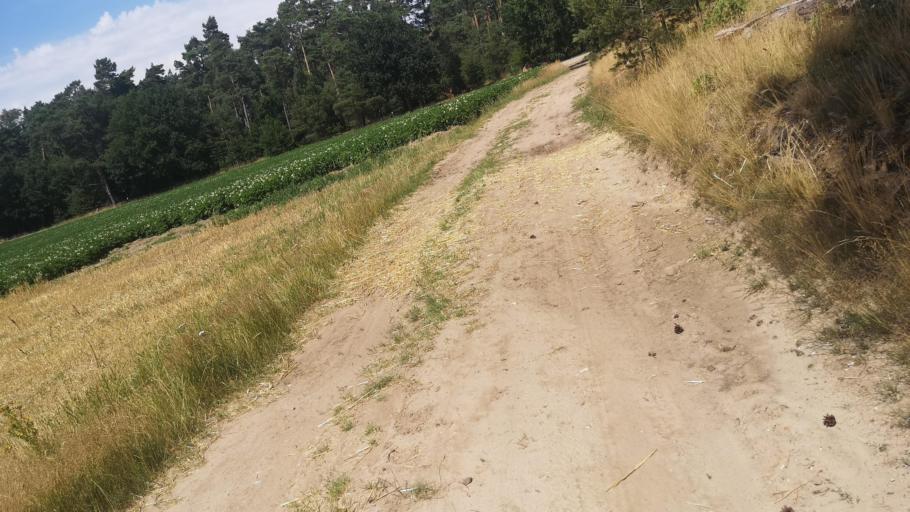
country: DE
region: Lower Saxony
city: Dahlem
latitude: 53.2274
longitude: 10.7230
